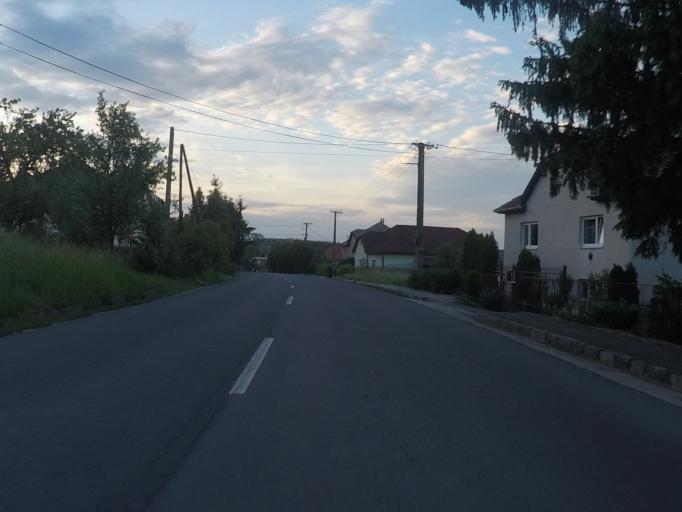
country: SK
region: Banskobystricky
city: Poltar
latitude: 48.3604
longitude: 19.8313
